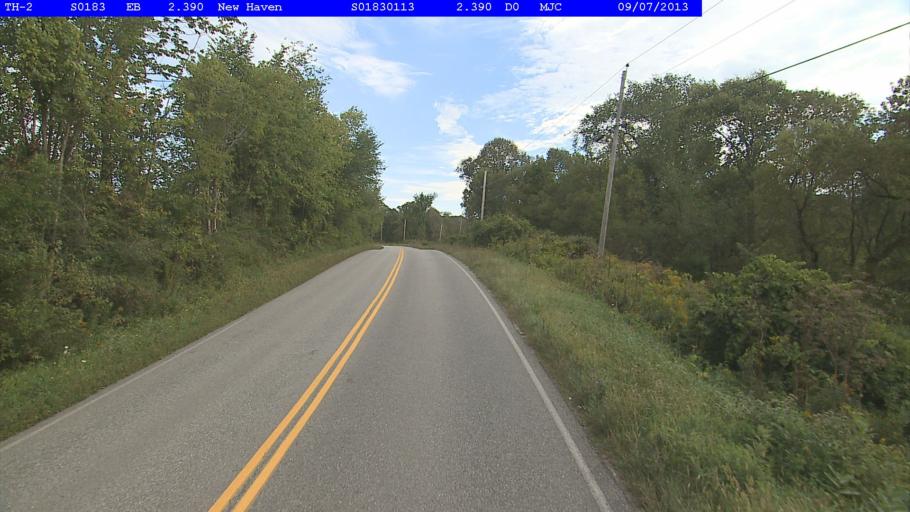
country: US
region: Vermont
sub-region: Addison County
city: Middlebury (village)
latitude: 44.0742
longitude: -73.1308
